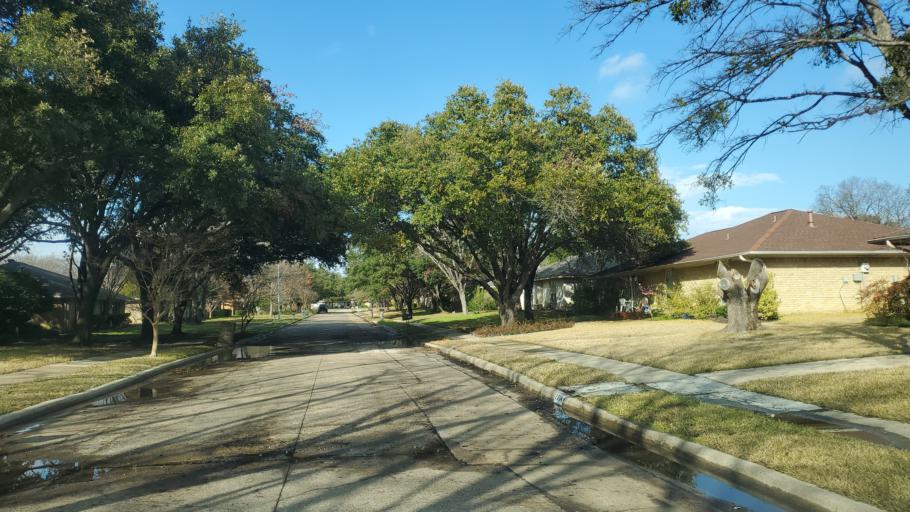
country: US
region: Texas
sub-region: Dallas County
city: Carrollton
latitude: 32.9793
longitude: -96.8959
